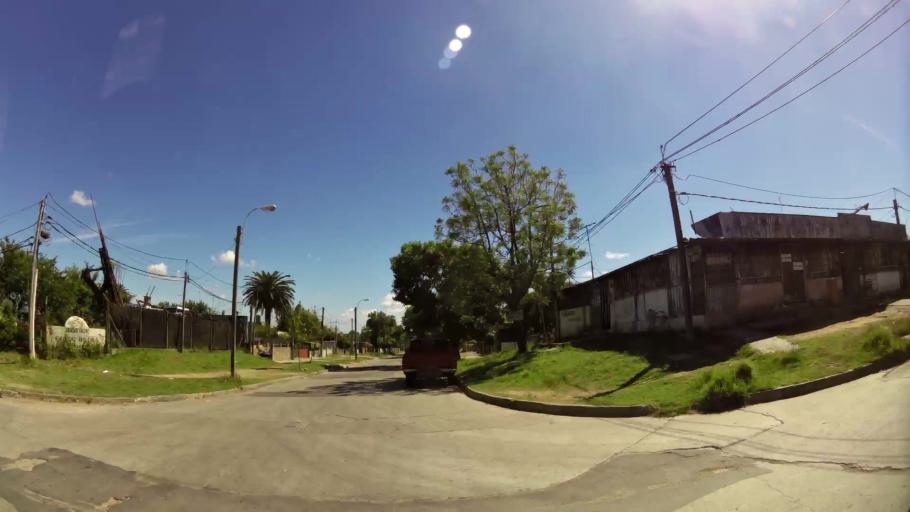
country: UY
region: Canelones
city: Paso de Carrasco
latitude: -34.8505
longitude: -56.1168
